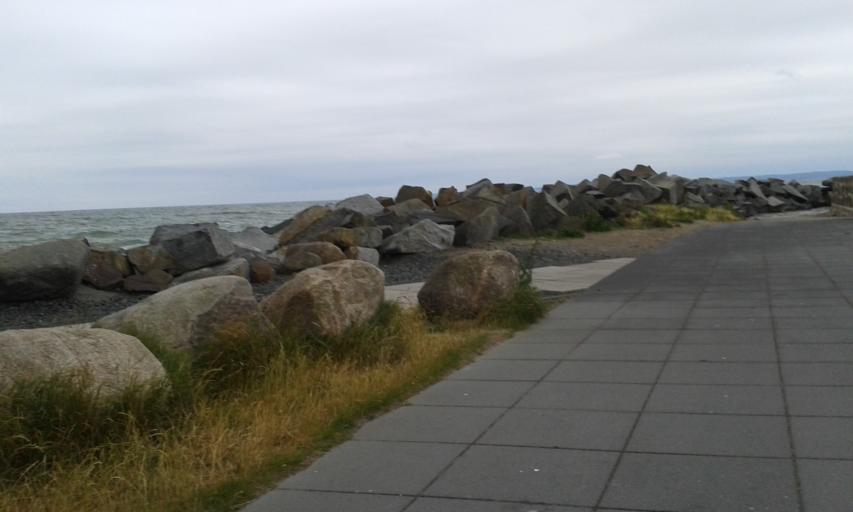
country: DE
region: Mecklenburg-Vorpommern
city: Sassnitz
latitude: 54.5144
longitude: 13.6509
